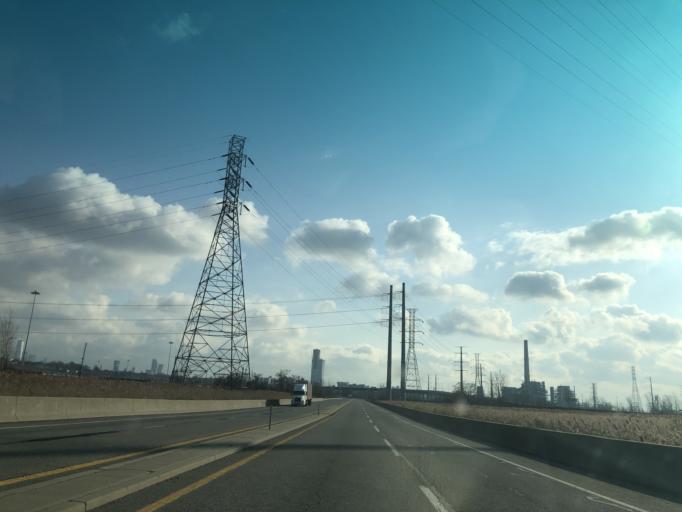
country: US
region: New Jersey
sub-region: Hudson County
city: Jersey City
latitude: 40.7588
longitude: -74.0717
